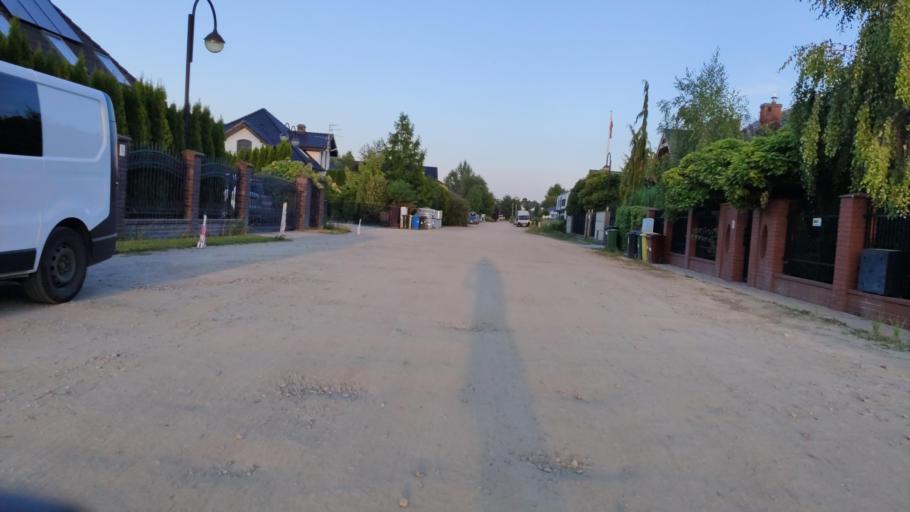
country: PL
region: Lower Silesian Voivodeship
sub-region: Powiat wroclawski
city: Zerniki Wroclawskie
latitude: 51.0649
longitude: 17.0606
